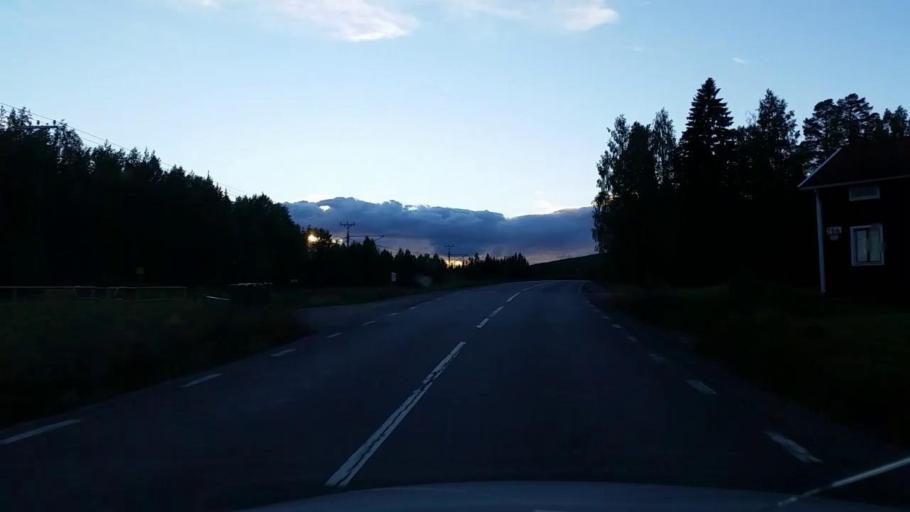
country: SE
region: Gaevleborg
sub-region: Ljusdals Kommun
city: Farila
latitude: 62.0810
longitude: 15.8168
